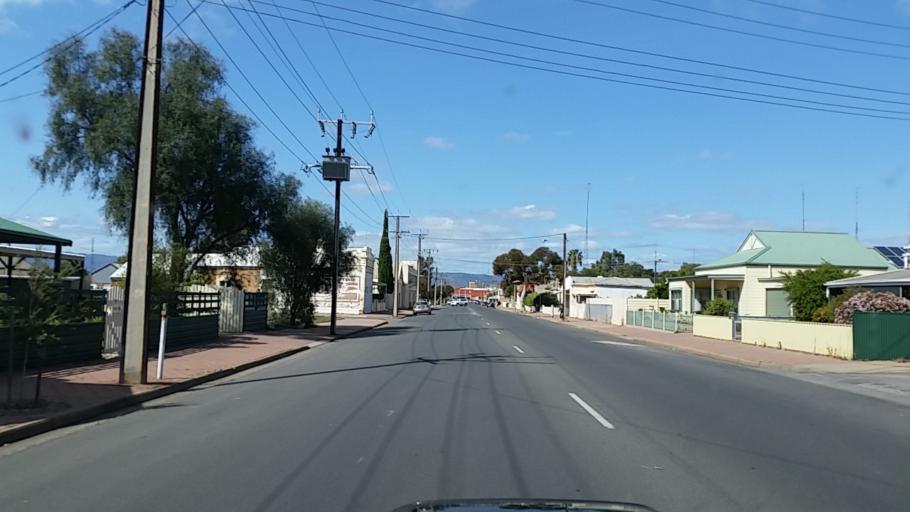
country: AU
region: South Australia
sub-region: Port Pirie City and Dists
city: Port Pirie
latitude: -33.1772
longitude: 137.9999
